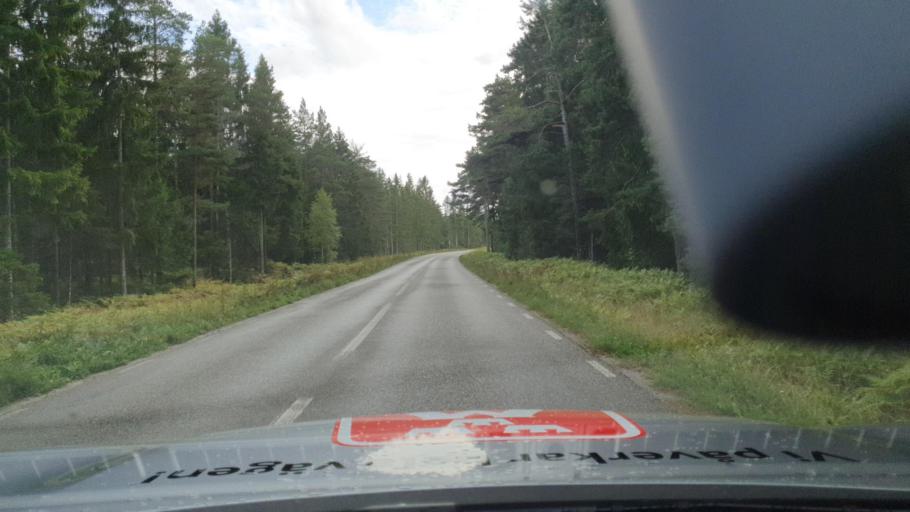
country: SE
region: Gotland
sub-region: Gotland
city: Slite
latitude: 57.6087
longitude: 18.7542
